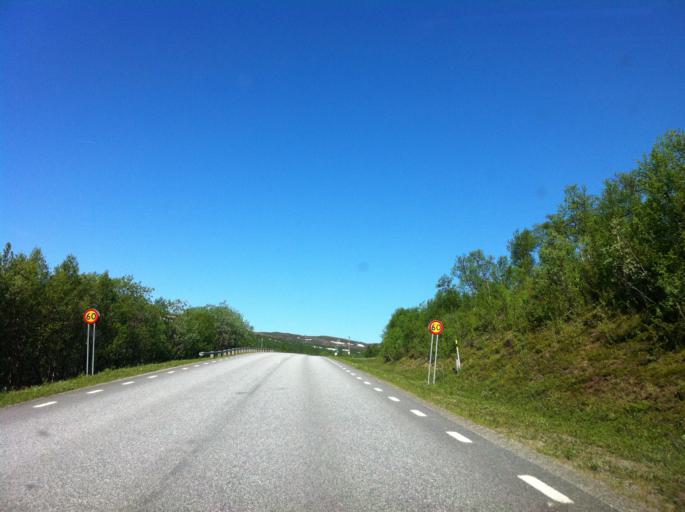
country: NO
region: Sor-Trondelag
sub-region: Tydal
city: Aas
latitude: 62.5562
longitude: 12.2749
